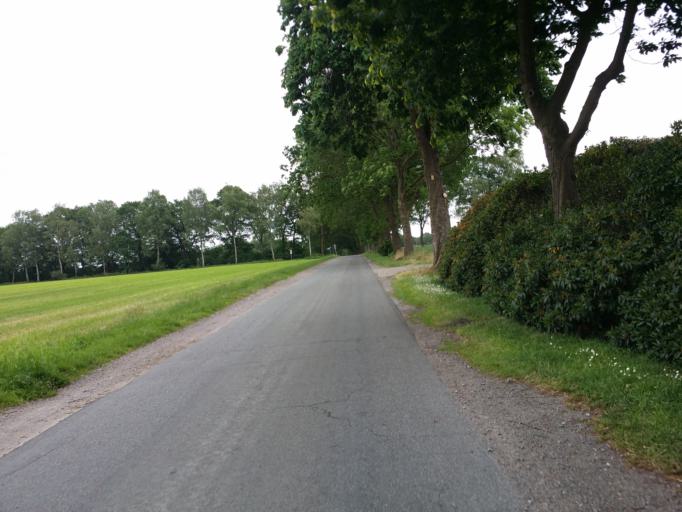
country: DE
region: Lower Saxony
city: Bockhorn
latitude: 53.3180
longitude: 8.0451
